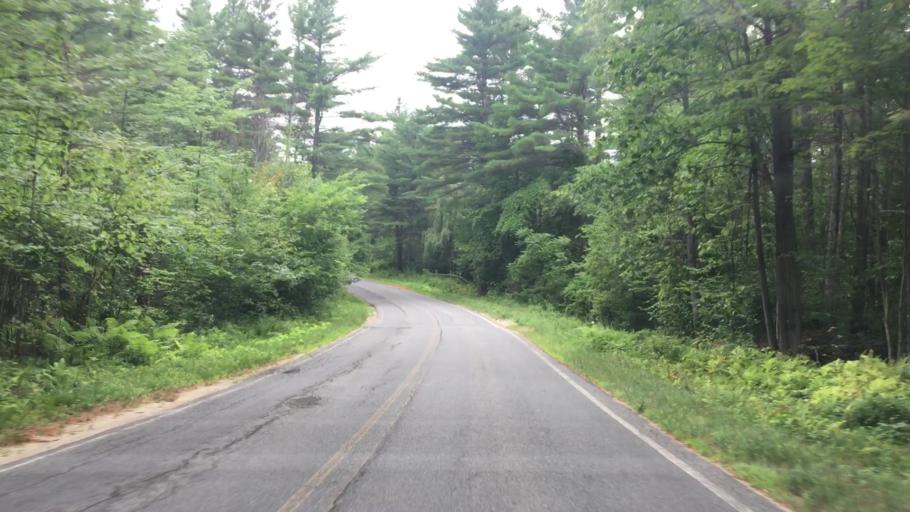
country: US
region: New York
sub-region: Essex County
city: Keeseville
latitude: 44.4417
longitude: -73.6119
